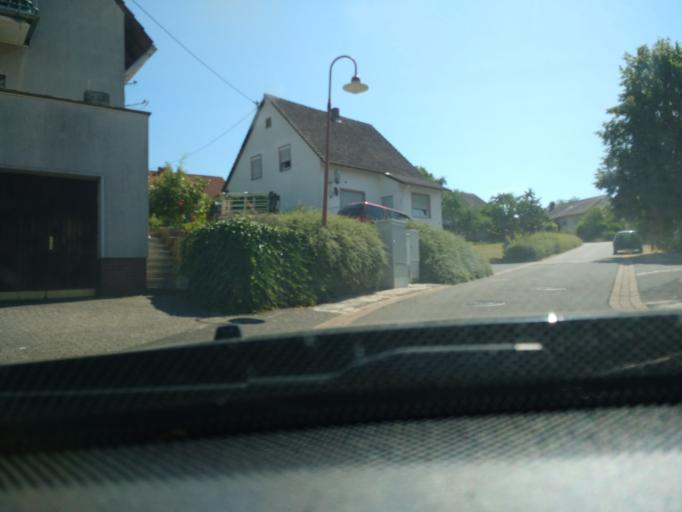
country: DE
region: Rheinland-Pfalz
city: Flussbach
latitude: 50.0161
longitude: 6.9291
